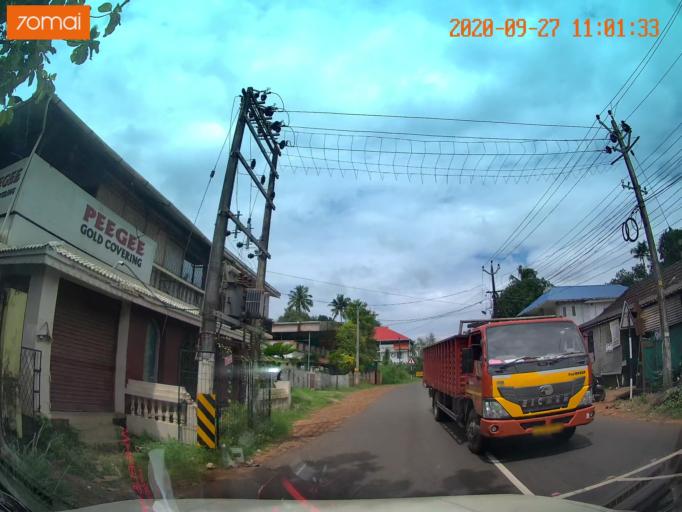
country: IN
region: Kerala
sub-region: Thrissur District
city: Irinjalakuda
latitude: 10.4200
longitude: 76.2660
